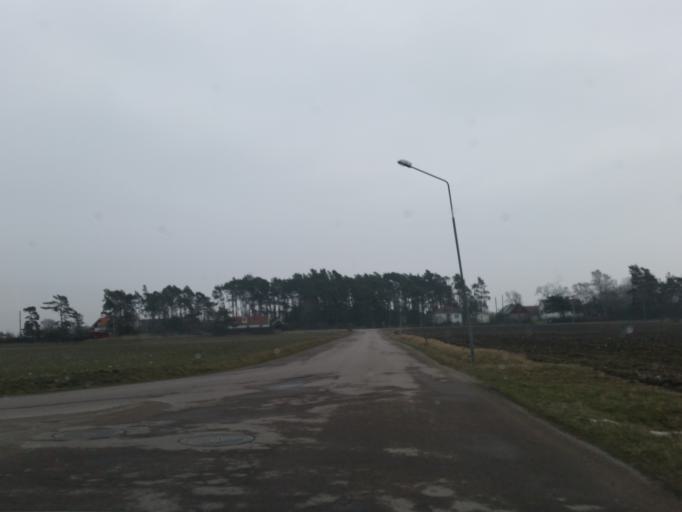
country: SE
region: Kalmar
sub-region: Morbylanga Kommun
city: Moerbylanga
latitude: 56.5085
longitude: 16.3902
